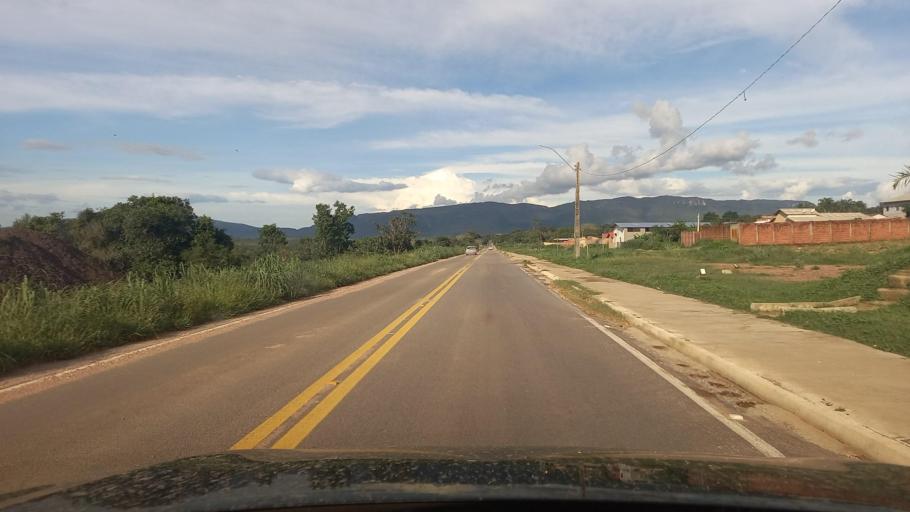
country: BR
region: Goias
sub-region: Cavalcante
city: Cavalcante
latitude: -13.7939
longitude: -47.4447
